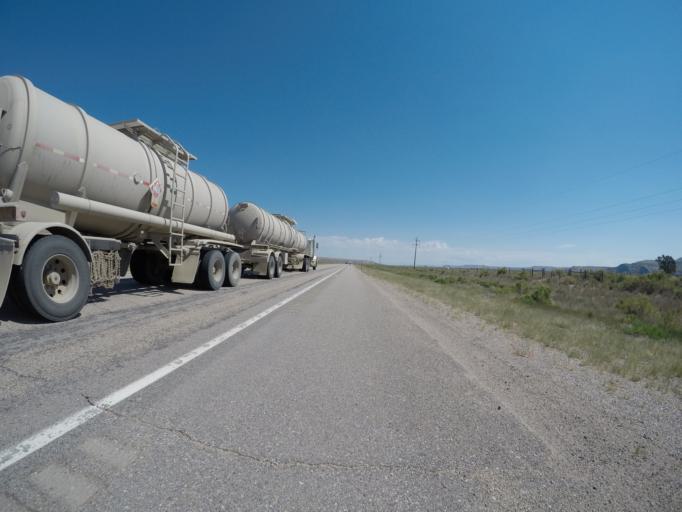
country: US
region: Wyoming
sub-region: Sublette County
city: Marbleton
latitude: 42.3470
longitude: -110.1618
